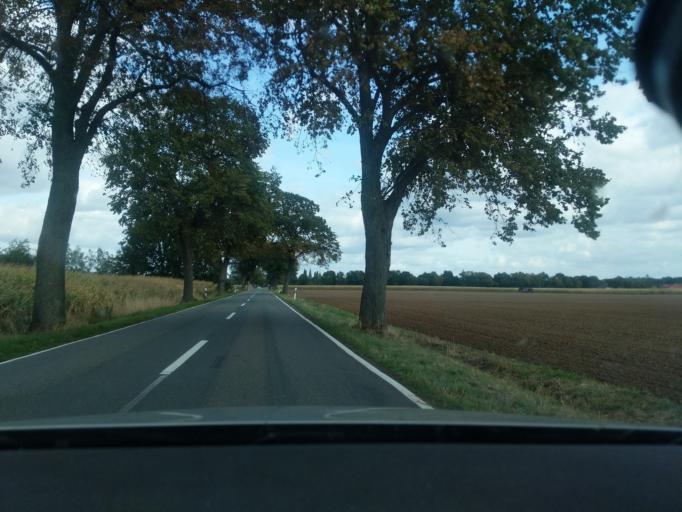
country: DE
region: Lower Saxony
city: Bucken
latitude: 52.7740
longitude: 9.1118
